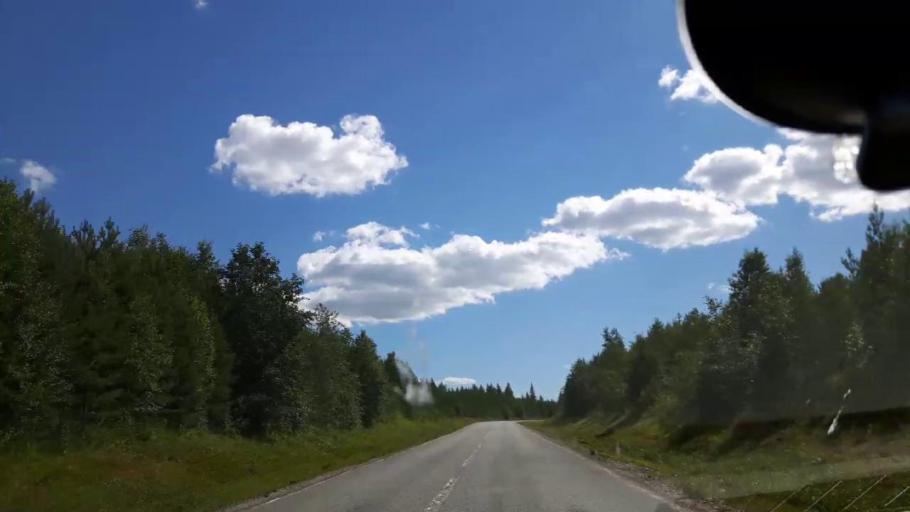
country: SE
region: Jaemtland
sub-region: Ragunda Kommun
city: Hammarstrand
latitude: 62.8649
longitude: 16.2142
